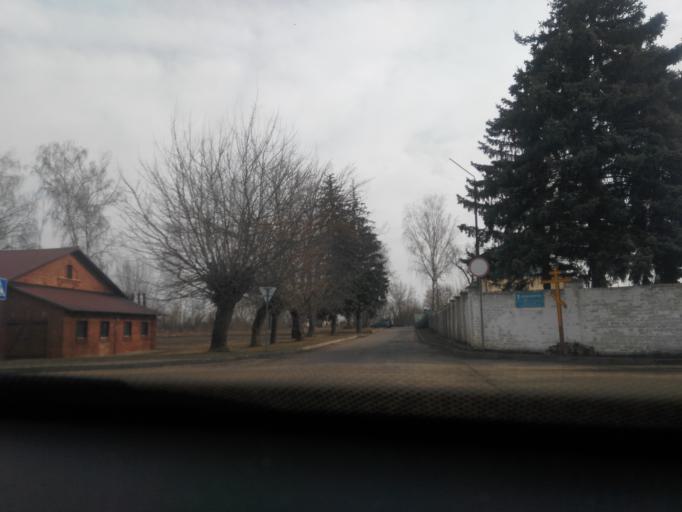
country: BY
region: Mogilev
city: Babruysk
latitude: 53.1395
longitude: 29.2466
